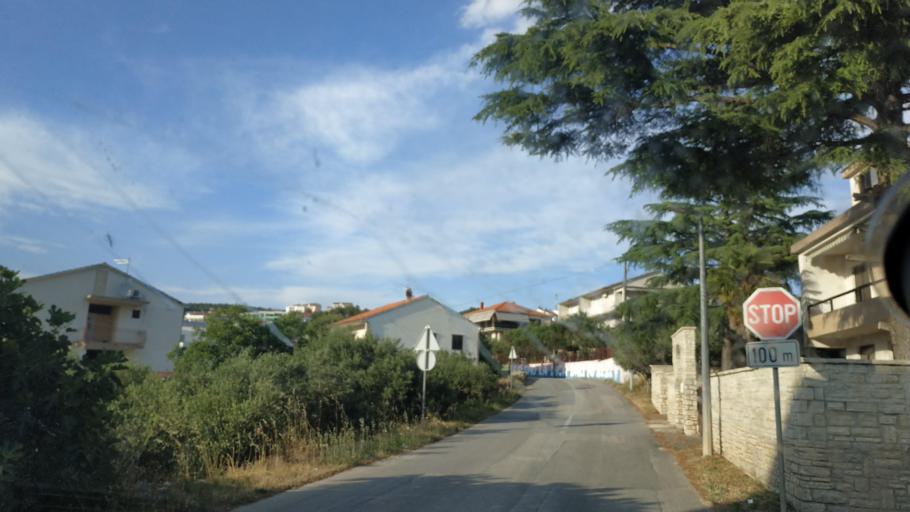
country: HR
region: Splitsko-Dalmatinska
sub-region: Grad Trogir
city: Trogir
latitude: 43.4950
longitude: 16.2616
